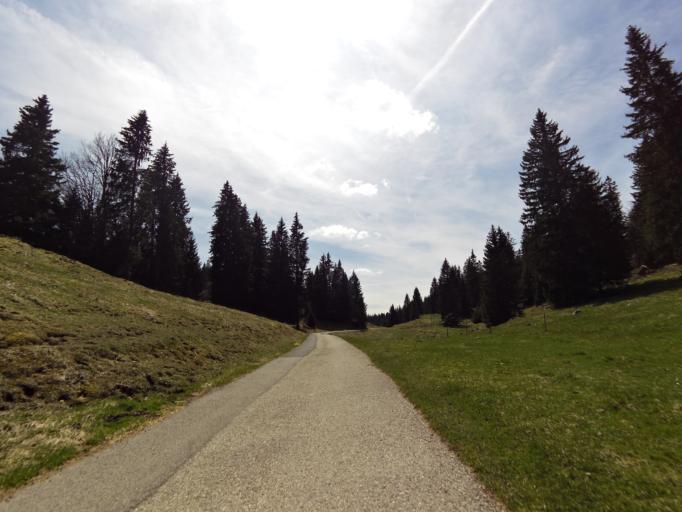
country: CH
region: Vaud
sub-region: Nyon District
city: Arzier
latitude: 46.5051
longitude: 6.1823
